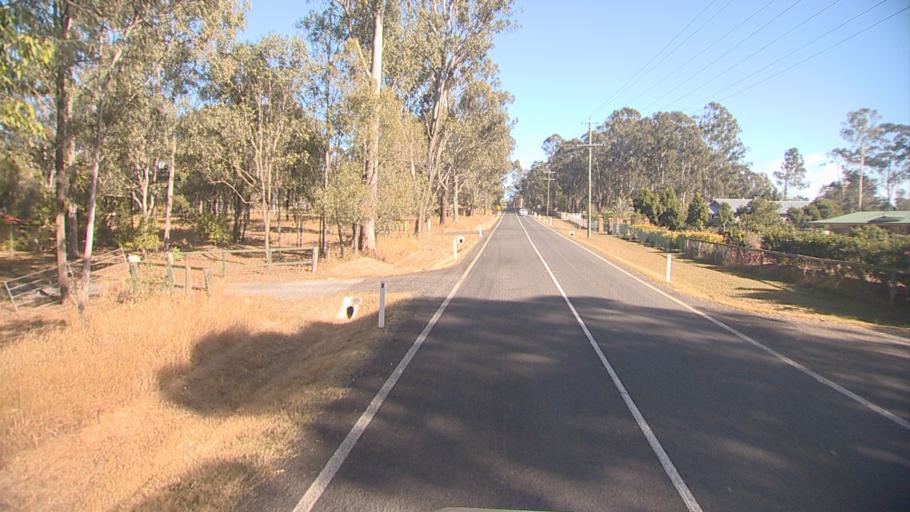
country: AU
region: Queensland
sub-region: Logan
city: Cedar Vale
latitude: -27.8622
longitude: 152.9881
